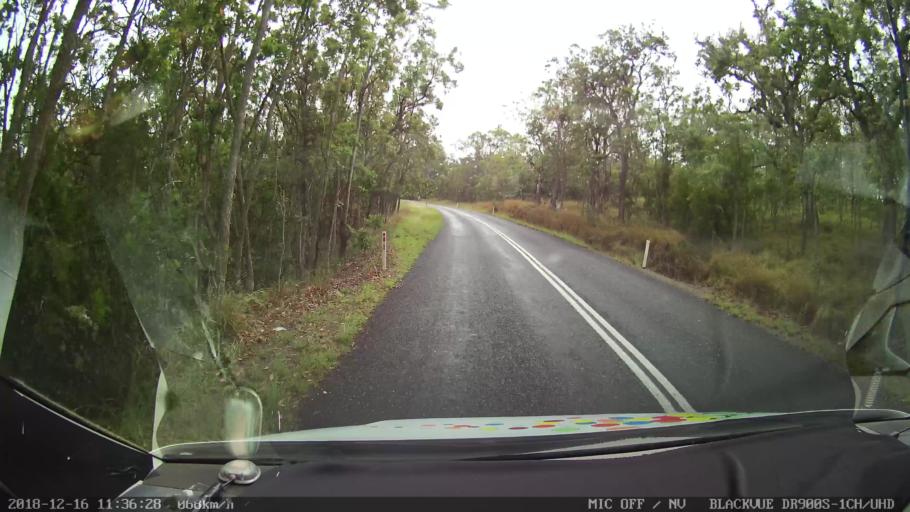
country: AU
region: New South Wales
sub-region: Tenterfield Municipality
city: Carrolls Creek
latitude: -28.9807
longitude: 152.1701
